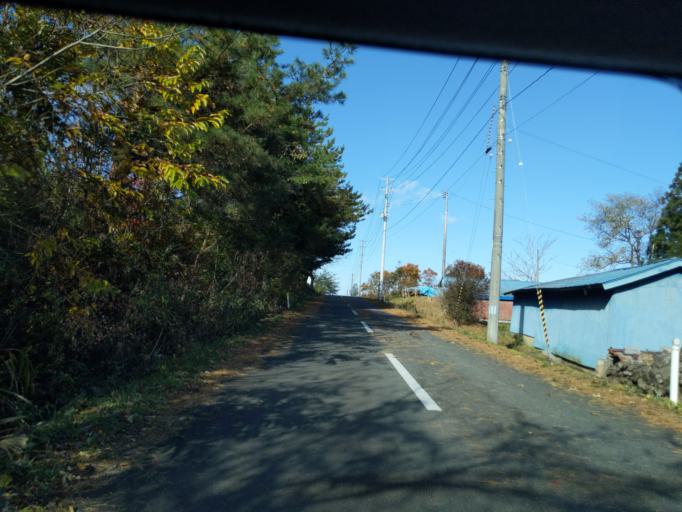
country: JP
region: Iwate
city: Mizusawa
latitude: 39.0619
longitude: 141.1128
